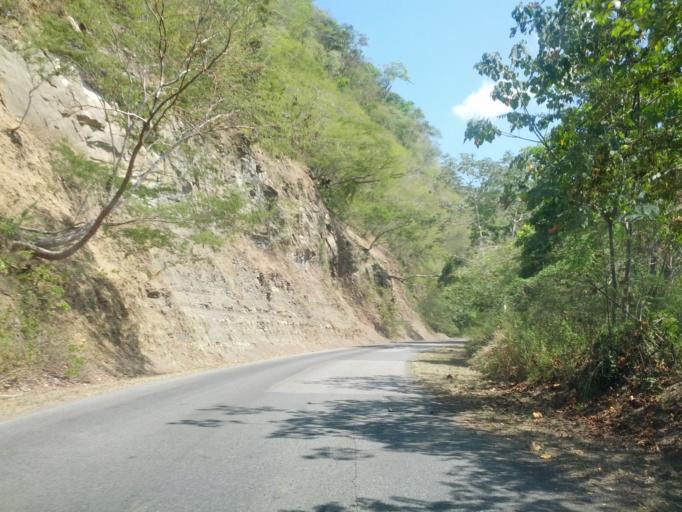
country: CR
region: Puntarenas
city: Ciudad Cortes
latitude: 8.9638
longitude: -83.3186
